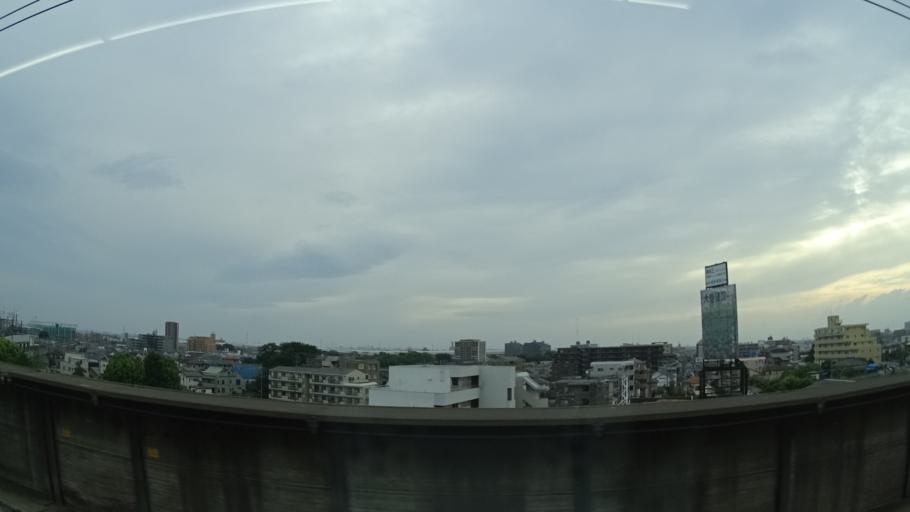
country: JP
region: Saitama
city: Yono
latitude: 35.8549
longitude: 139.6363
